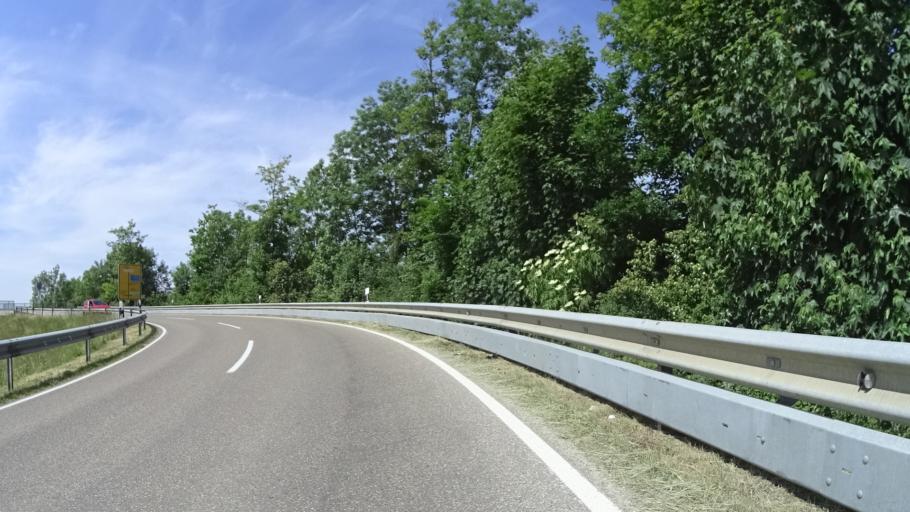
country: DE
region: Bavaria
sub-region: Lower Bavaria
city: Bad Abbach
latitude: 48.9288
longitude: 12.0143
